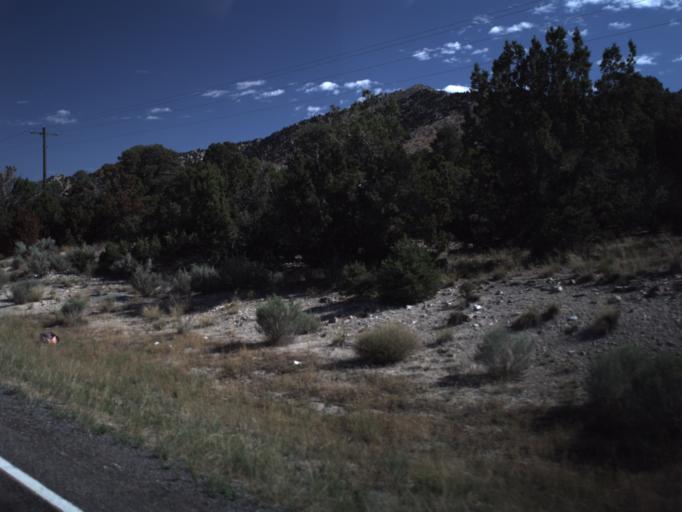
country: US
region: Utah
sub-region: Juab County
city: Mona
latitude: 39.9193
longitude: -112.1443
